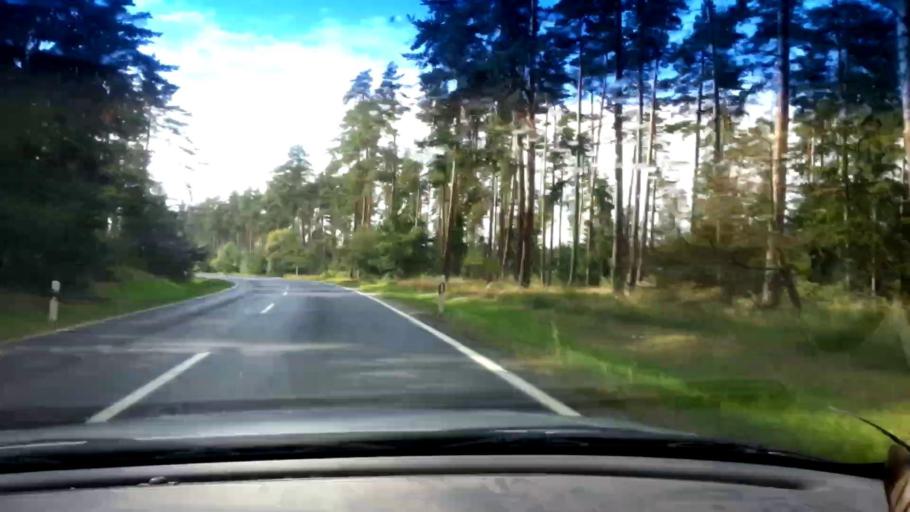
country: DE
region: Bavaria
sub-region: Upper Palatinate
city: Mitterteich
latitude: 49.9961
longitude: 12.2213
